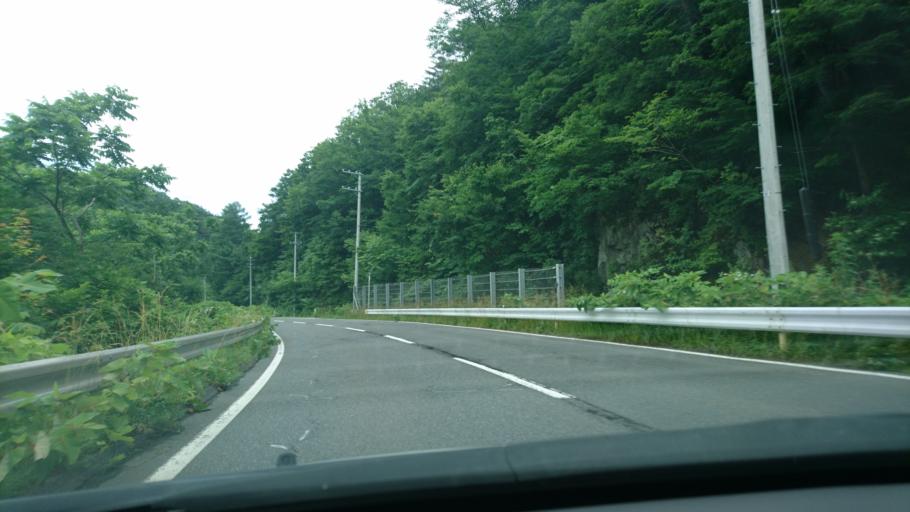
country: JP
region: Iwate
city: Miyako
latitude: 39.9883
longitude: 141.8696
